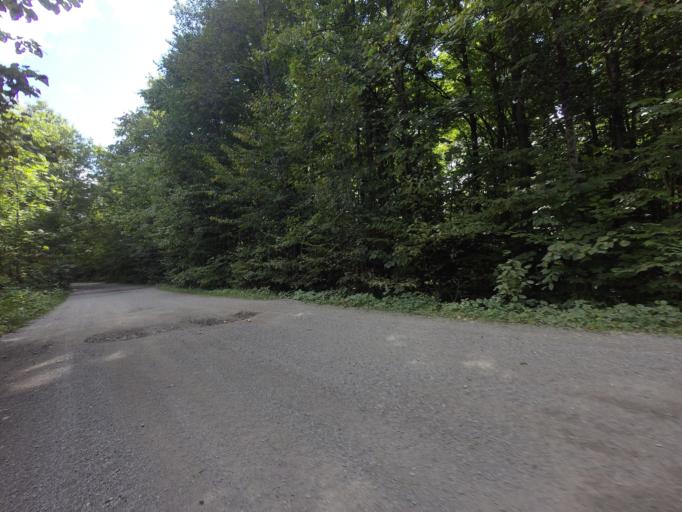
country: CA
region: Ontario
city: Omemee
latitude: 44.7615
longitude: -78.6634
